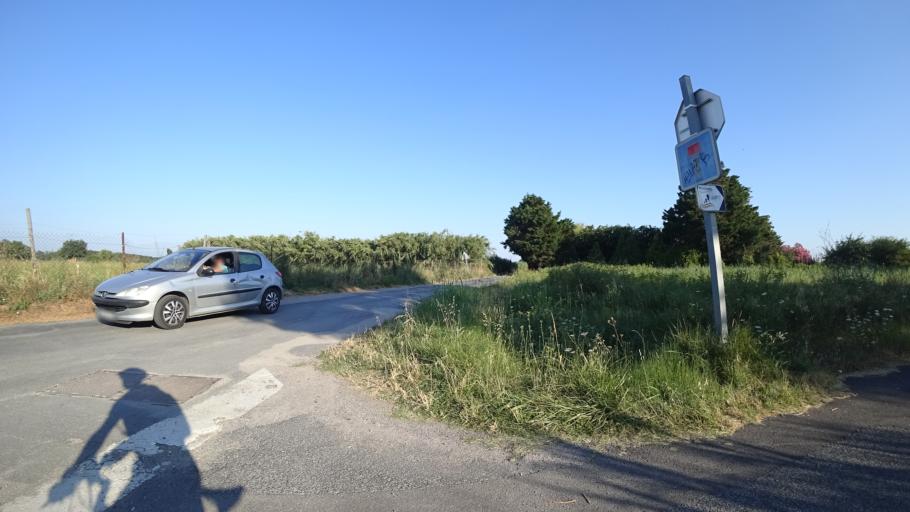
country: FR
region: Languedoc-Roussillon
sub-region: Departement des Pyrenees-Orientales
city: Sainte-Marie-Plage
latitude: 42.7163
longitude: 3.0276
